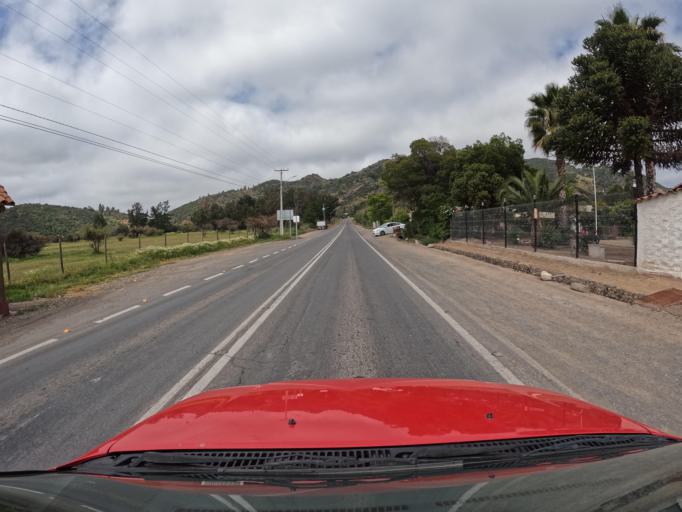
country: CL
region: O'Higgins
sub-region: Provincia de Colchagua
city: Santa Cruz
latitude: -34.6588
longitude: -71.4105
